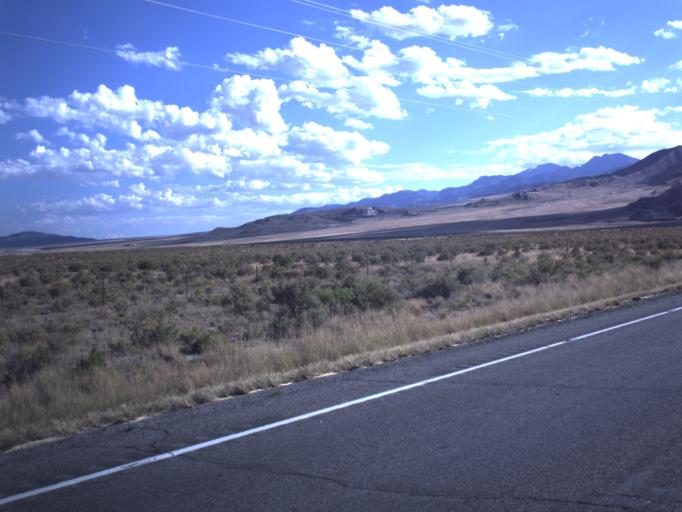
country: US
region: Utah
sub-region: Tooele County
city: Grantsville
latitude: 40.6917
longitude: -112.5358
